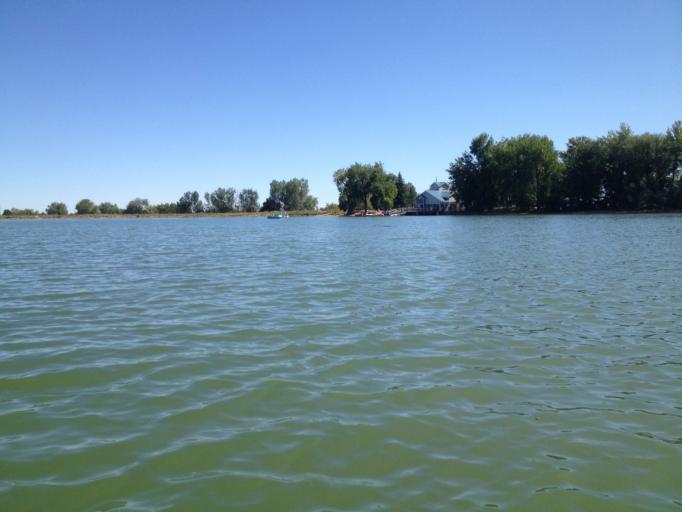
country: US
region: Colorado
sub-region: Boulder County
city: Louisville
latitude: 39.9946
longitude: -105.1149
